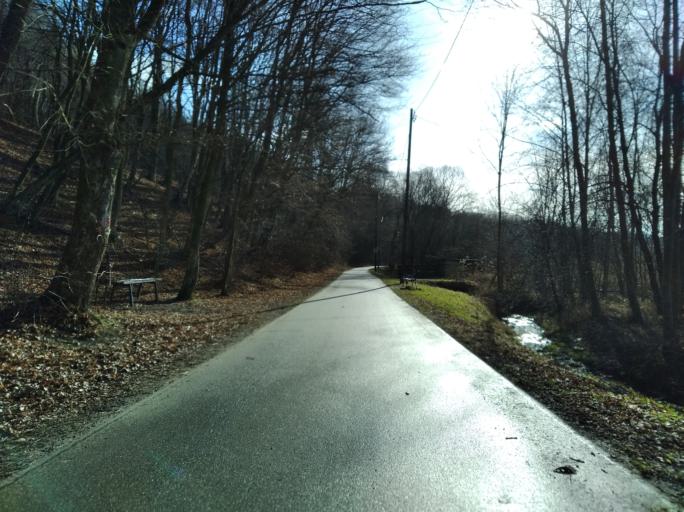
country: PL
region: Subcarpathian Voivodeship
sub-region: Powiat strzyzowski
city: Strzyzow
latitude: 49.8771
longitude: 21.7777
